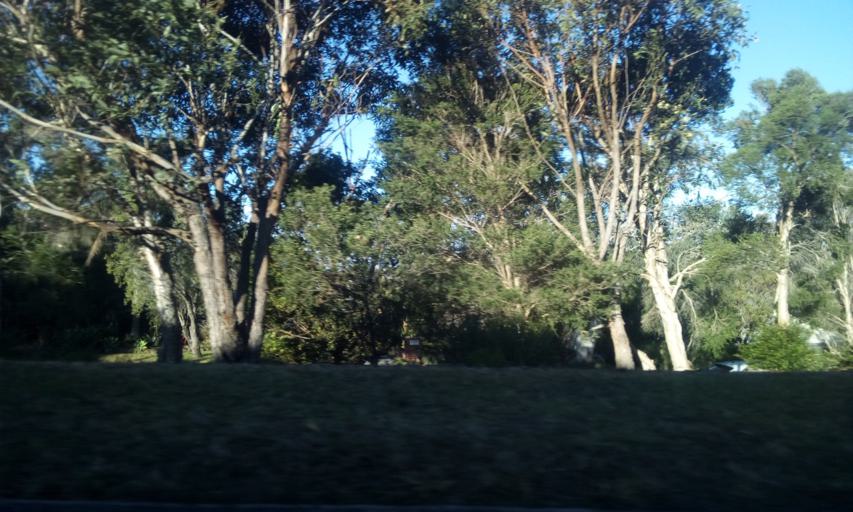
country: AU
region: New South Wales
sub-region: Wollongong
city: Mount Keira
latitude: -34.4235
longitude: 150.8505
